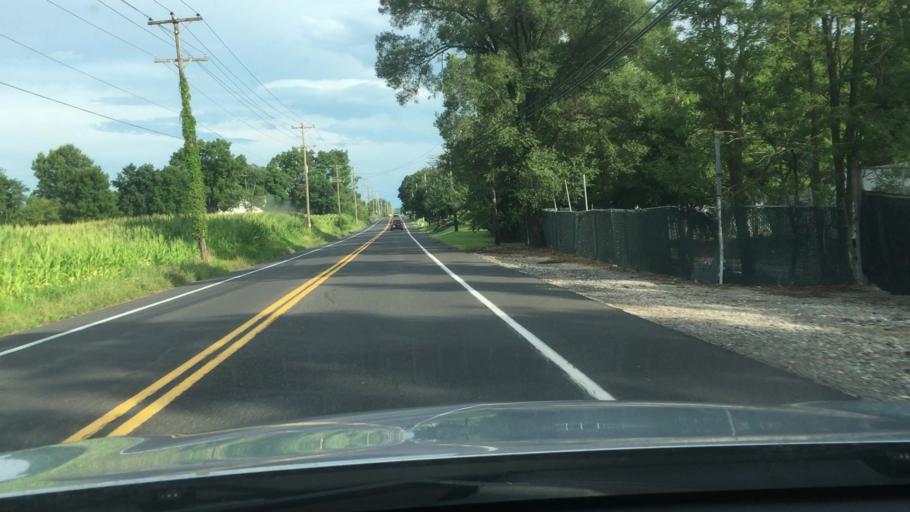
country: US
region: Pennsylvania
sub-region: York County
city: Dover
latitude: 40.0180
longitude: -76.8660
